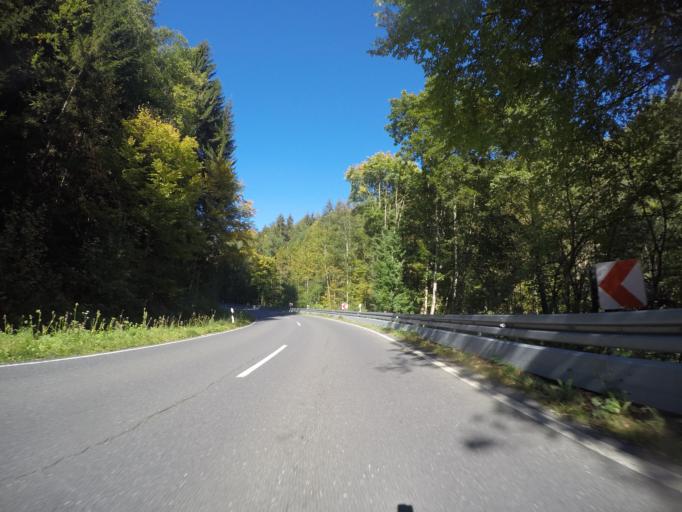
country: DE
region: Bavaria
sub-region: Upper Franconia
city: Gossweinstein
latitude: 49.7989
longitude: 11.3315
